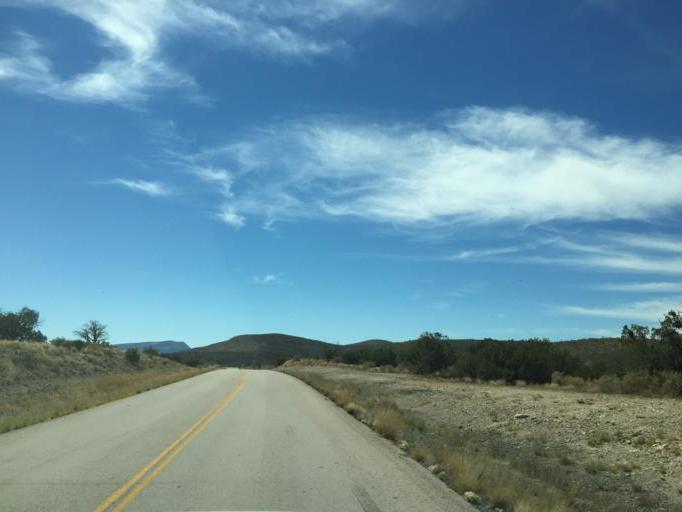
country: US
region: Arizona
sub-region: Mohave County
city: Meadview
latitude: 35.9371
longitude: -113.9000
